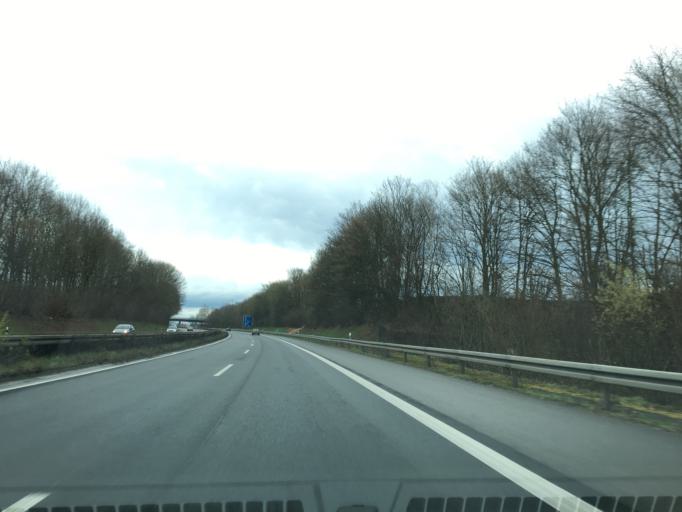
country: DE
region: North Rhine-Westphalia
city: Erkelenz
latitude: 51.0714
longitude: 6.3308
